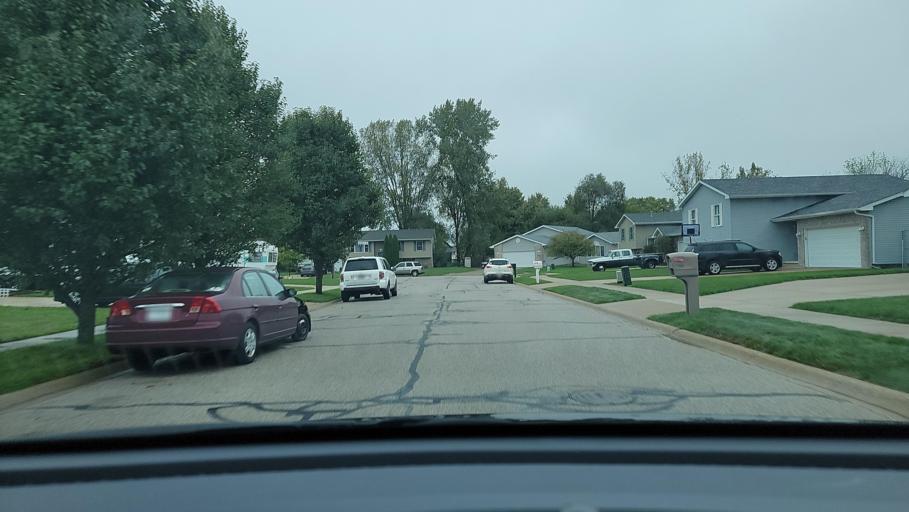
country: US
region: Indiana
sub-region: Porter County
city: Portage
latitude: 41.5445
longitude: -87.1876
